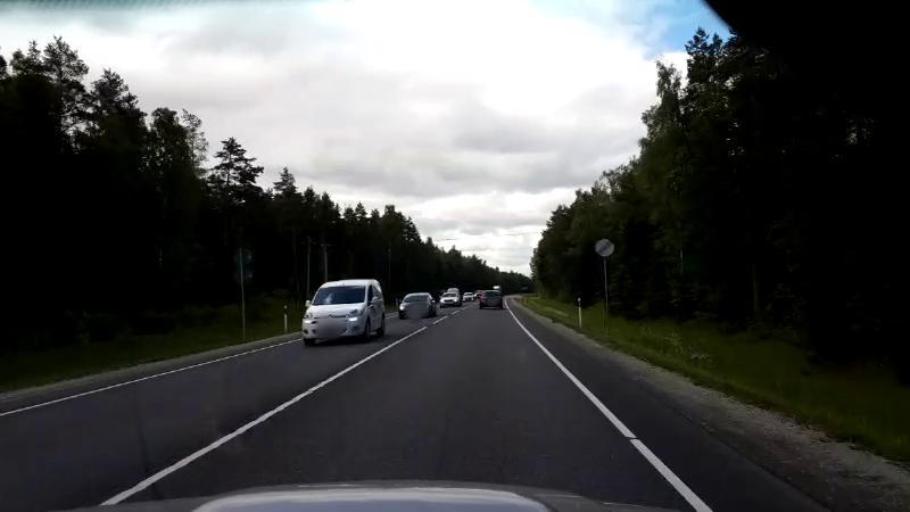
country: EE
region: Raplamaa
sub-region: Maerjamaa vald
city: Marjamaa
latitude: 58.8913
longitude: 24.4543
